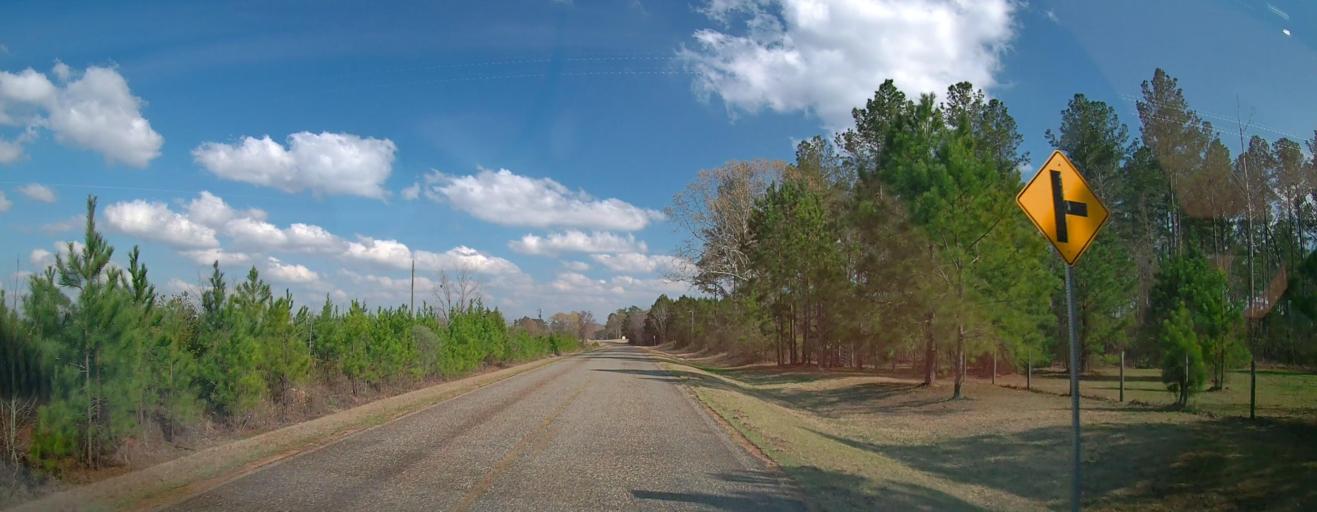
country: US
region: Georgia
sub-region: Twiggs County
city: Jeffersonville
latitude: 32.6435
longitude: -83.1867
